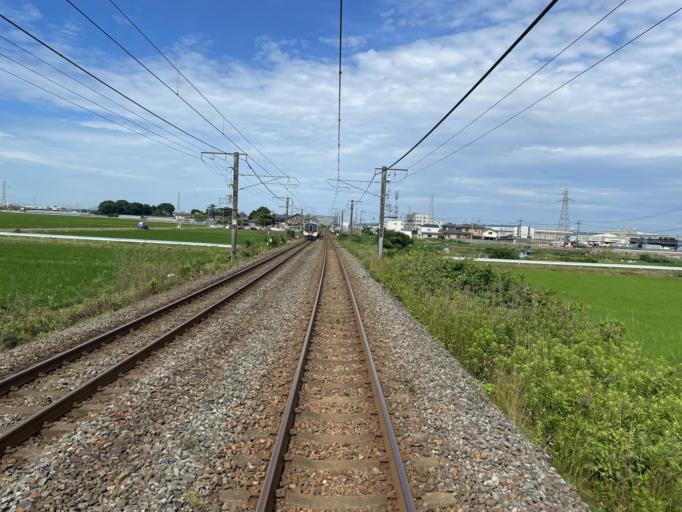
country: JP
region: Niigata
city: Kameda-honcho
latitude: 37.9163
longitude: 139.1325
